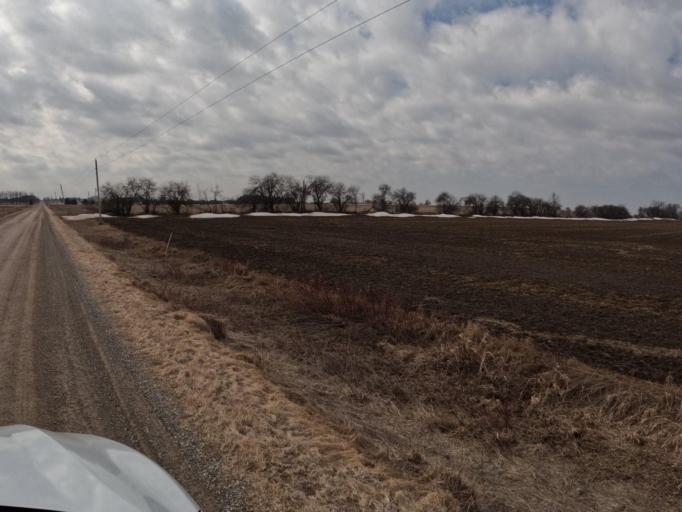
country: CA
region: Ontario
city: Orangeville
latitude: 43.9323
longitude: -80.2421
